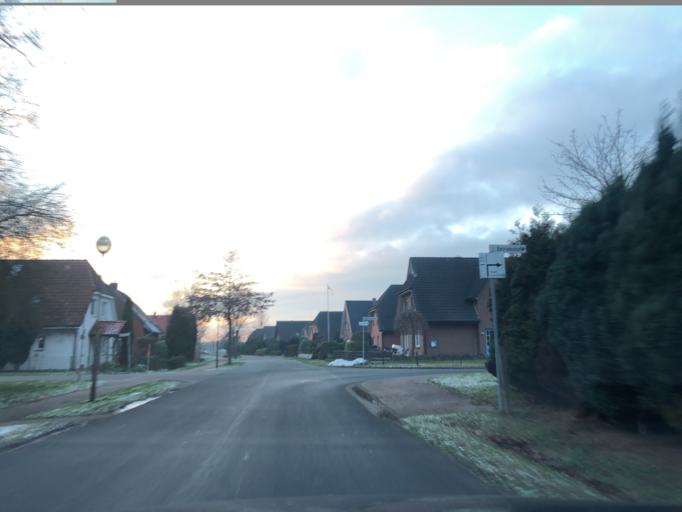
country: DE
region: Lower Saxony
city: Lemwerder
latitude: 53.1610
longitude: 8.6009
